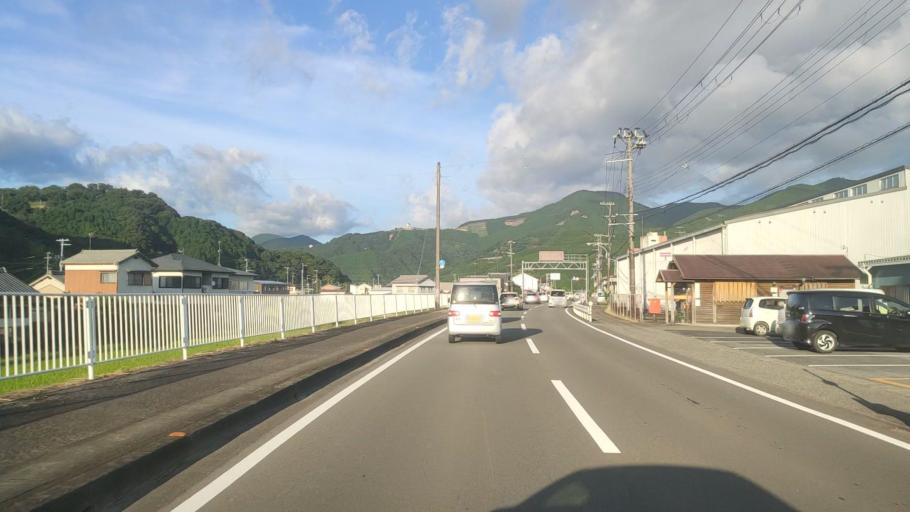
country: JP
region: Wakayama
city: Tanabe
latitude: 33.7159
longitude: 135.4620
